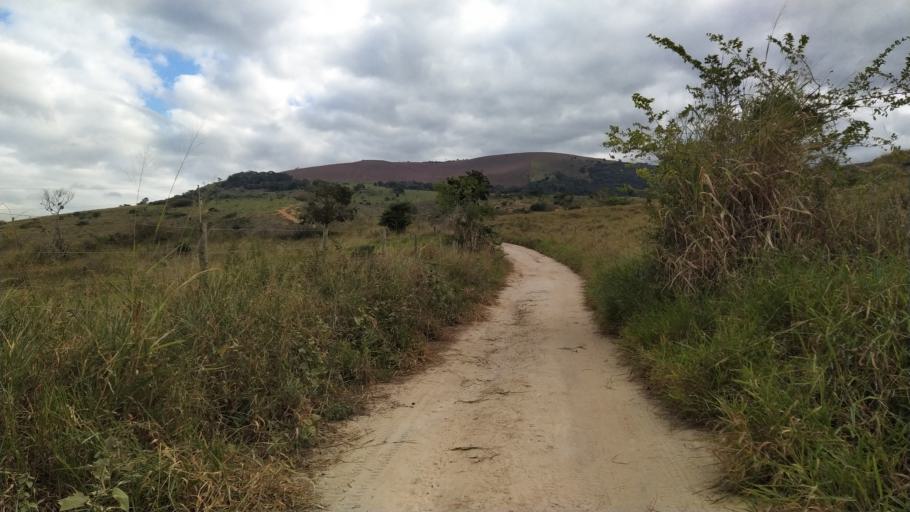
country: BR
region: Minas Gerais
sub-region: Almenara
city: Almenara
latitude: -16.6294
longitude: -40.4585
